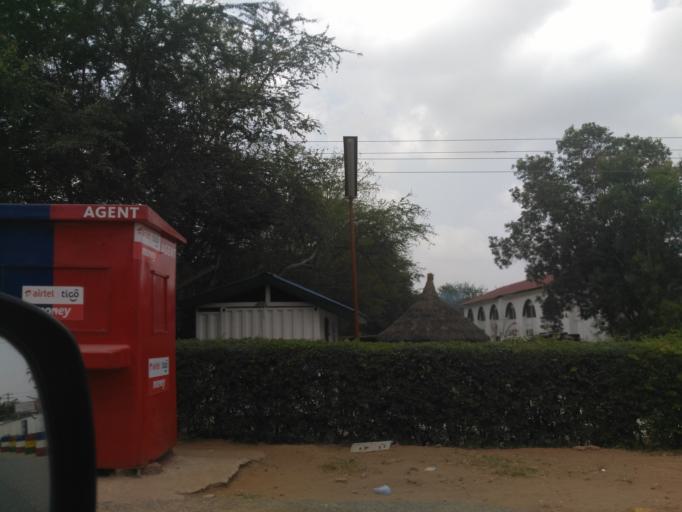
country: GH
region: Greater Accra
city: Accra
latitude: 5.5967
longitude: -0.1818
